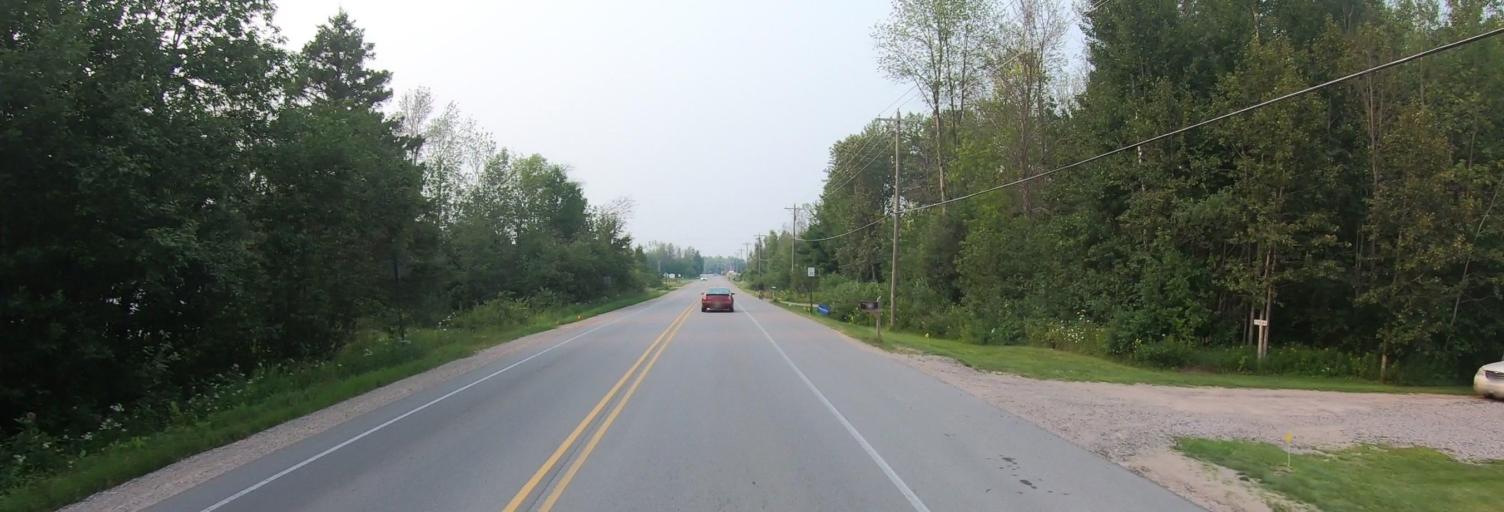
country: US
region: Michigan
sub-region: Chippewa County
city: Sault Ste. Marie
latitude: 46.4180
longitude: -84.6038
